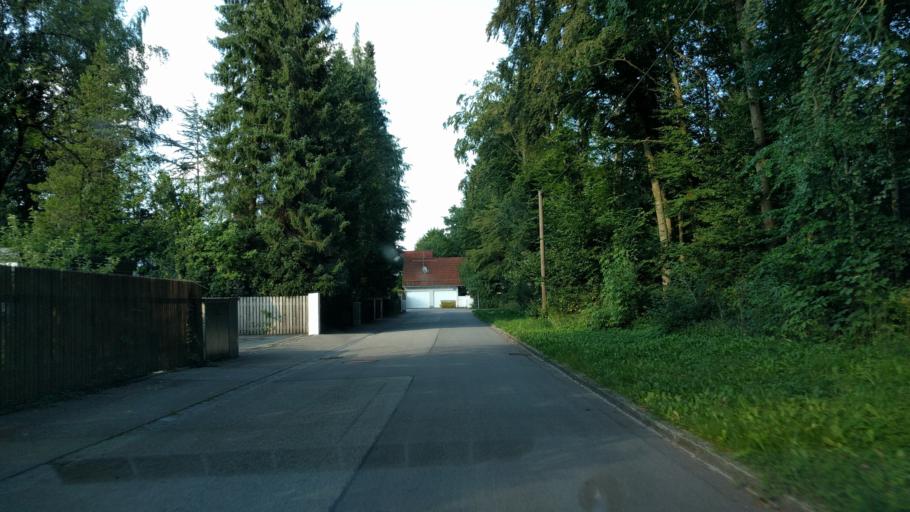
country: DE
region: Bavaria
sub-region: Upper Bavaria
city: Grunwald
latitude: 48.0323
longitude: 11.5328
